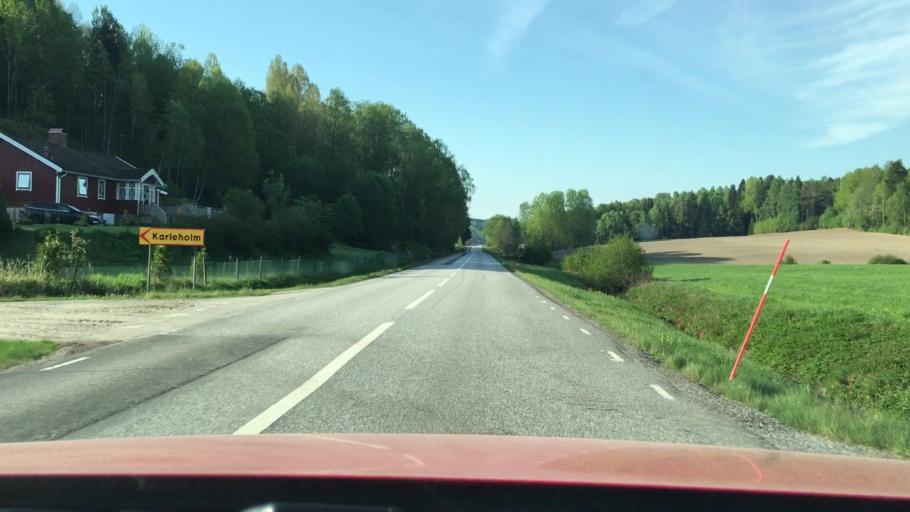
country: SE
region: Vaestra Goetaland
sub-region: Munkedals Kommun
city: Munkedal
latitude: 58.6180
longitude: 11.5585
